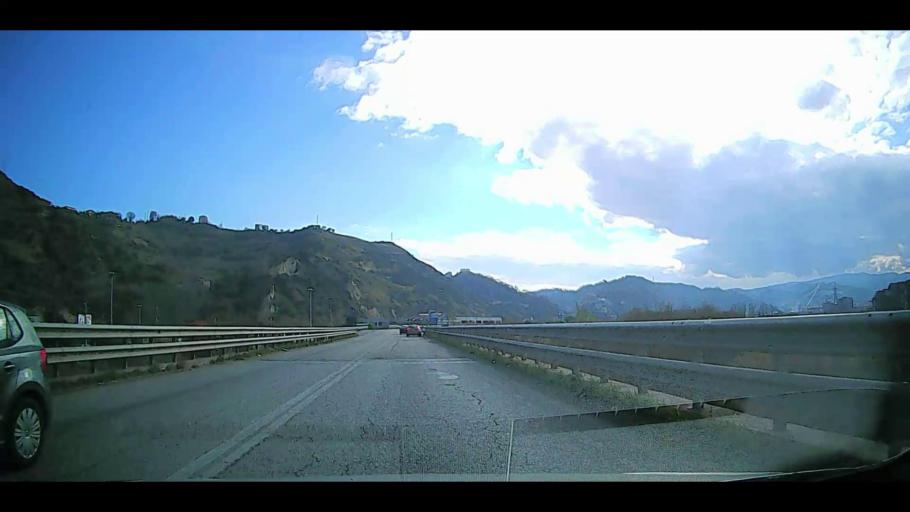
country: IT
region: Calabria
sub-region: Provincia di Cosenza
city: Cosenza
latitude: 39.3120
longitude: 16.2612
